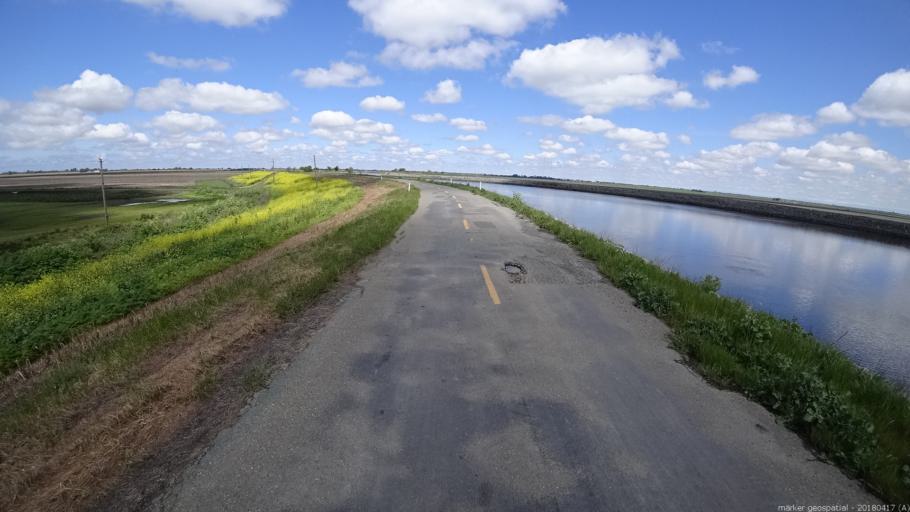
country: US
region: California
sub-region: Sacramento County
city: Walnut Grove
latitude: 38.1739
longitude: -121.5252
